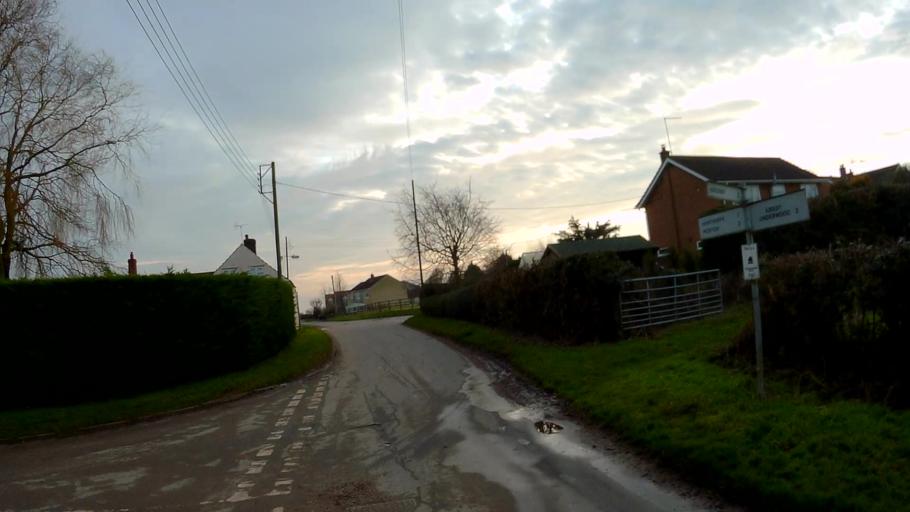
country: GB
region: England
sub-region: Lincolnshire
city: Bourne
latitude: 52.8130
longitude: -0.3987
